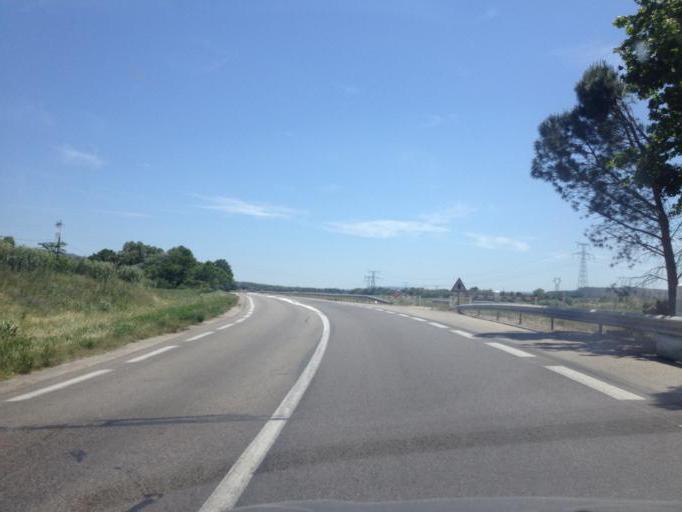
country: FR
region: Provence-Alpes-Cote d'Azur
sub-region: Departement du Vaucluse
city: Cavaillon
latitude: 43.8378
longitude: 5.0163
